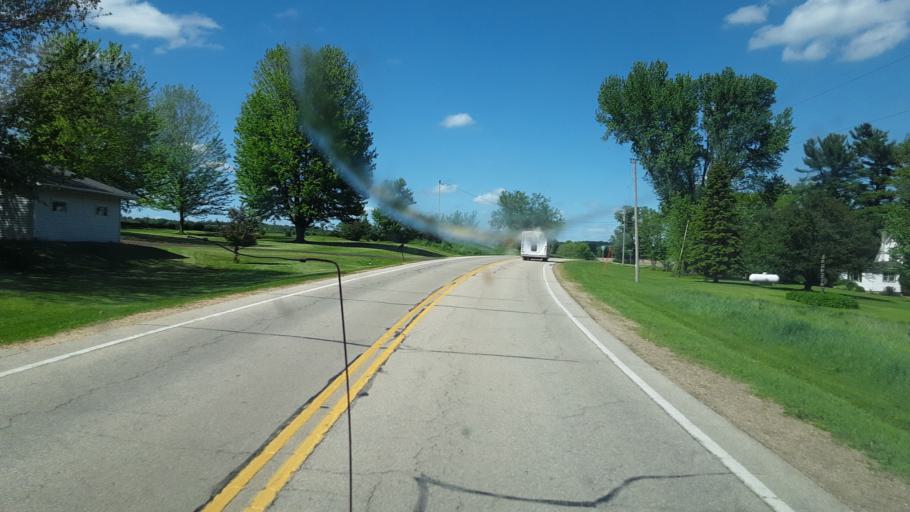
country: US
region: Wisconsin
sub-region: Vernon County
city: Hillsboro
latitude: 43.5174
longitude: -90.2061
